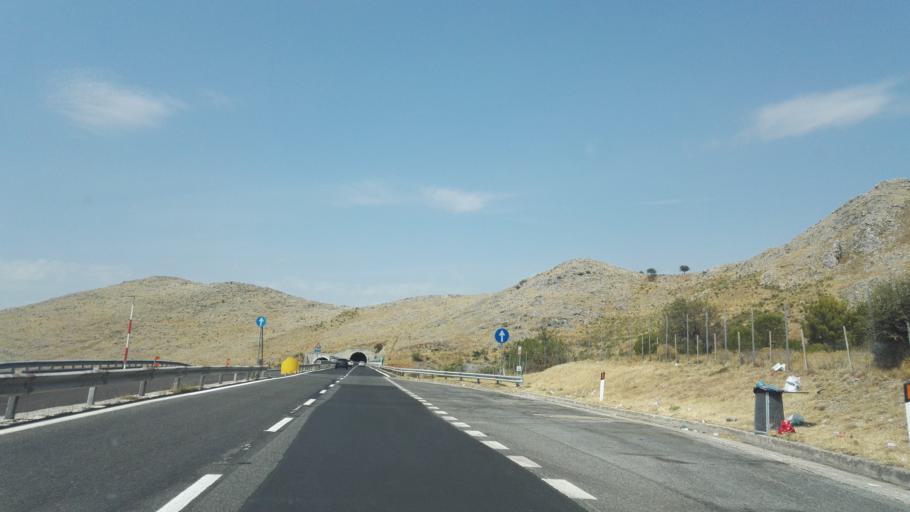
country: IT
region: Calabria
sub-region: Provincia di Cosenza
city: Castrovillari
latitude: 39.8485
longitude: 16.2179
